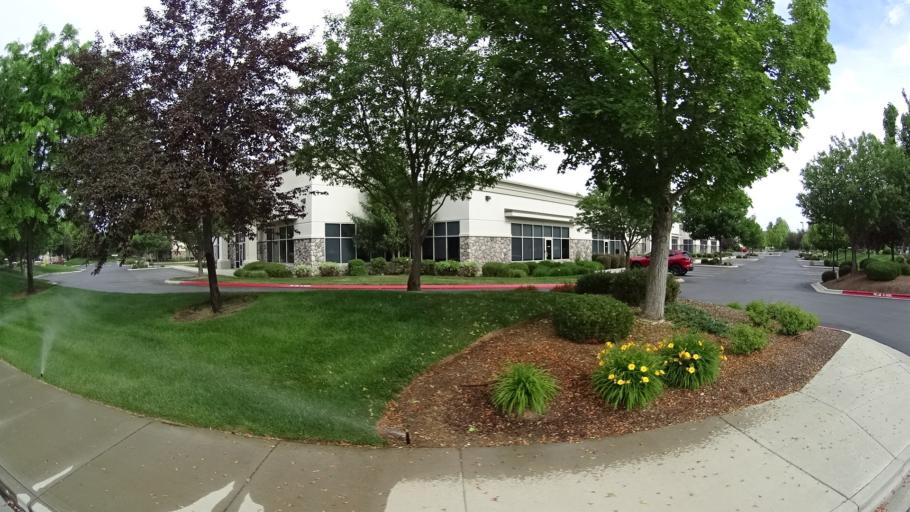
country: US
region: Idaho
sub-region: Ada County
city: Meridian
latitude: 43.5858
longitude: -116.3520
